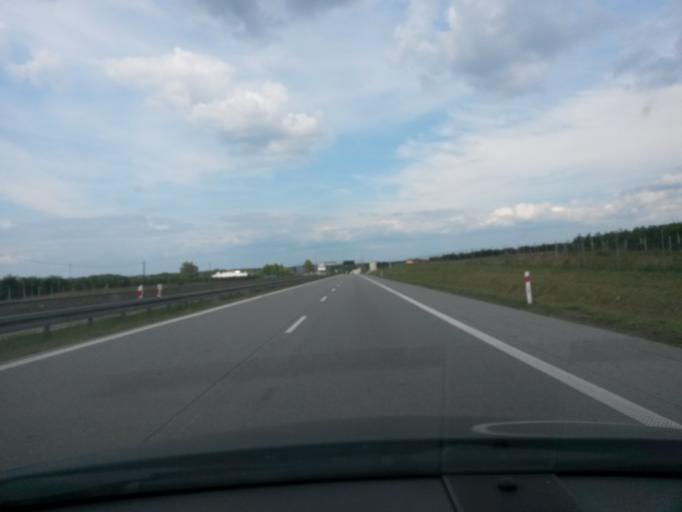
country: PL
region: Lodz Voivodeship
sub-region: Powiat skierniewicki
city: Kowiesy
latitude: 51.8815
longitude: 20.4036
